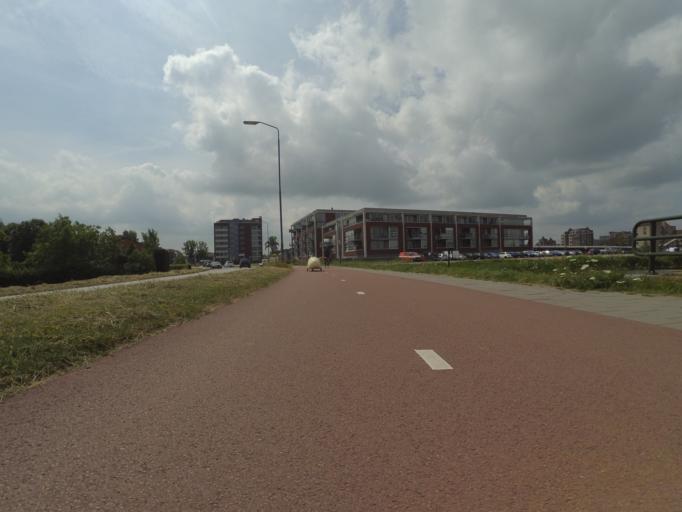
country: NL
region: North Brabant
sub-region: Gemeente Geertruidenberg
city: Geertruidenberg
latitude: 51.7013
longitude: 4.8692
